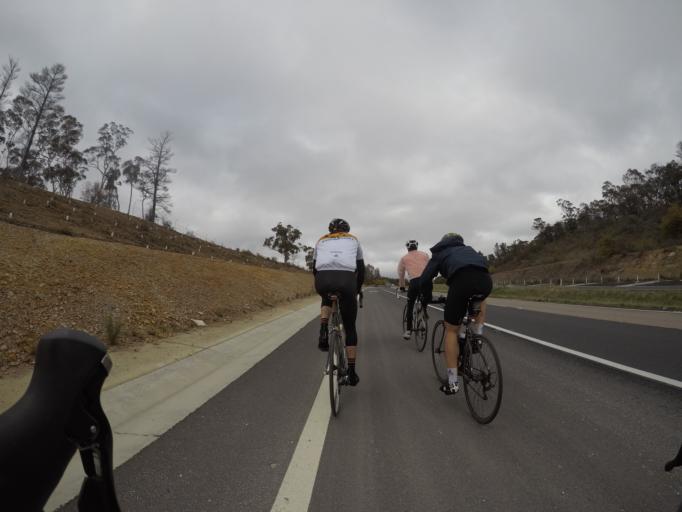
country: AU
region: New South Wales
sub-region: Lithgow
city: Lithgow
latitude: -33.4333
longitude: 150.0727
